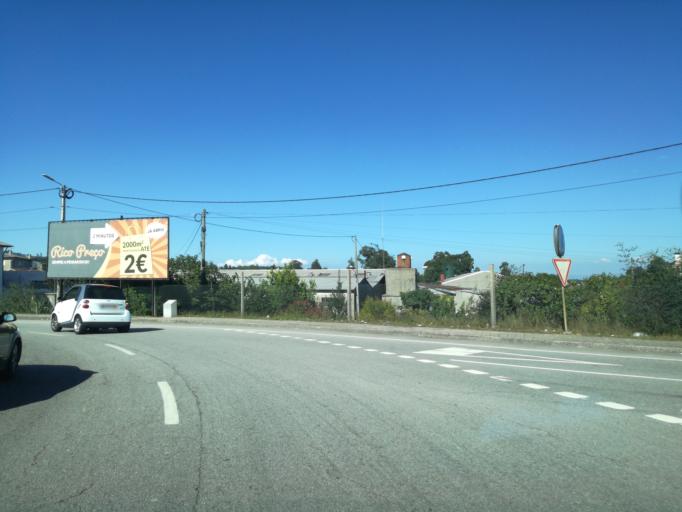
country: PT
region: Porto
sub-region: Pacos de Ferreira
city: Seroa
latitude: 41.2573
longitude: -8.4417
